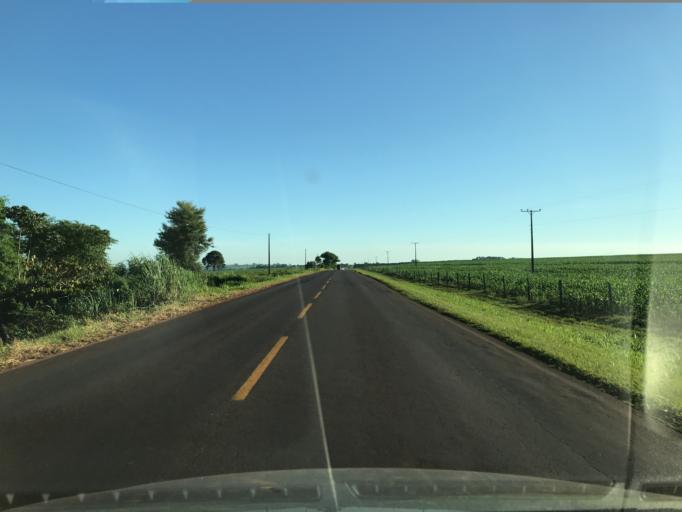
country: BR
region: Parana
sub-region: Palotina
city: Palotina
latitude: -24.1140
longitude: -53.8459
